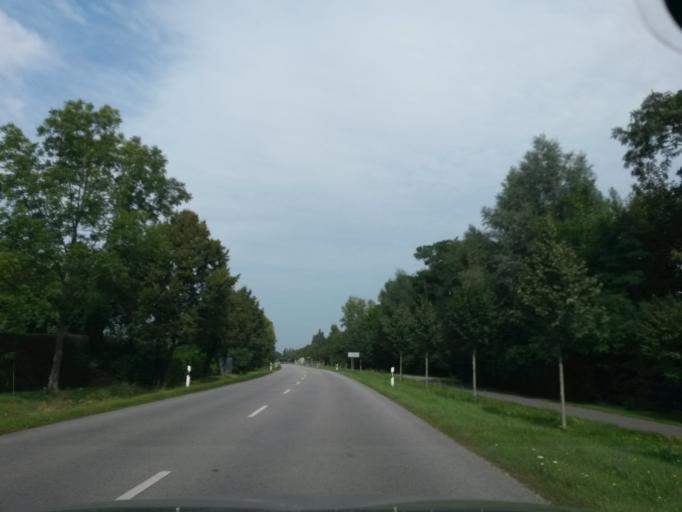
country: DE
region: Brandenburg
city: Schwedt (Oder)
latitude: 53.0515
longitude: 14.2714
